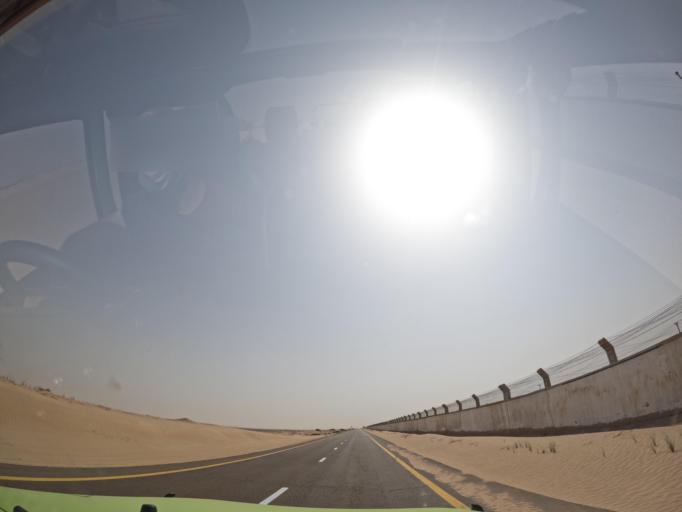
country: AE
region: Dubai
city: Dubai
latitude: 24.6140
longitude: 55.3213
